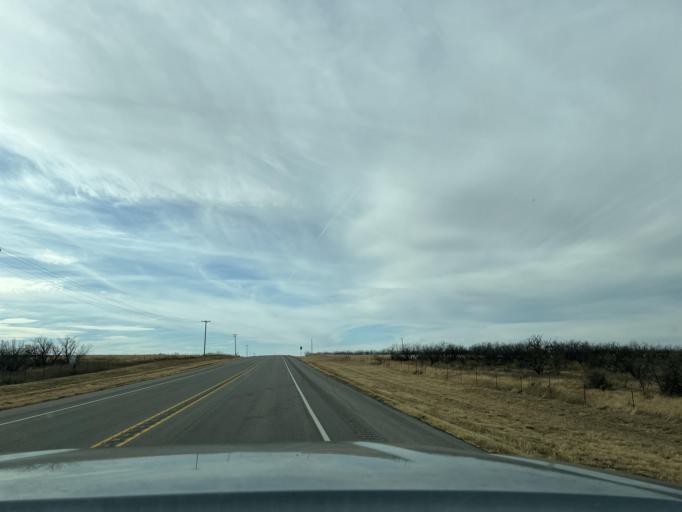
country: US
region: Texas
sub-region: Jones County
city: Anson
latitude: 32.7506
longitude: -99.6861
